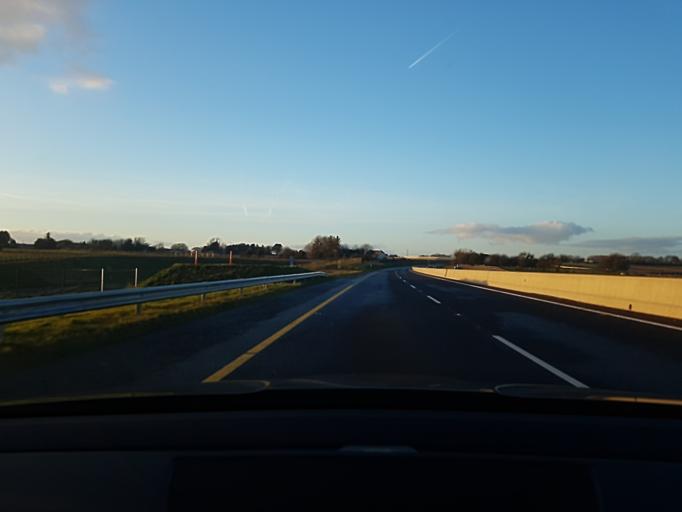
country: IE
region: Connaught
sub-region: County Galway
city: Tuam
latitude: 53.4320
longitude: -8.8414
